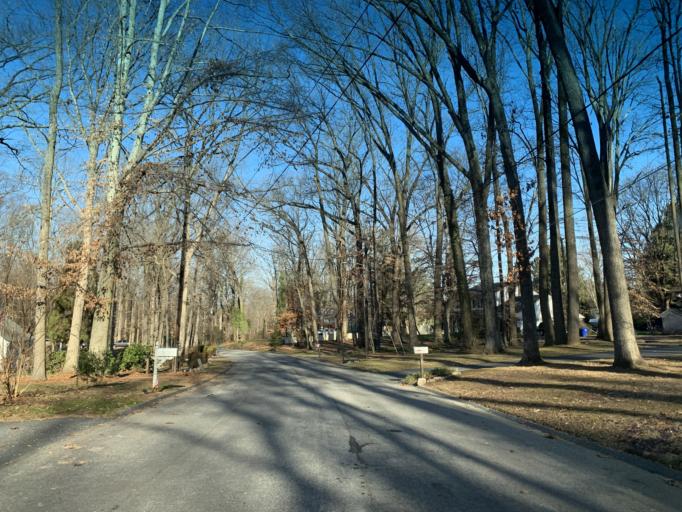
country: US
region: Maryland
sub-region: Harford County
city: Riverside
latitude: 39.5720
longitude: -76.2470
